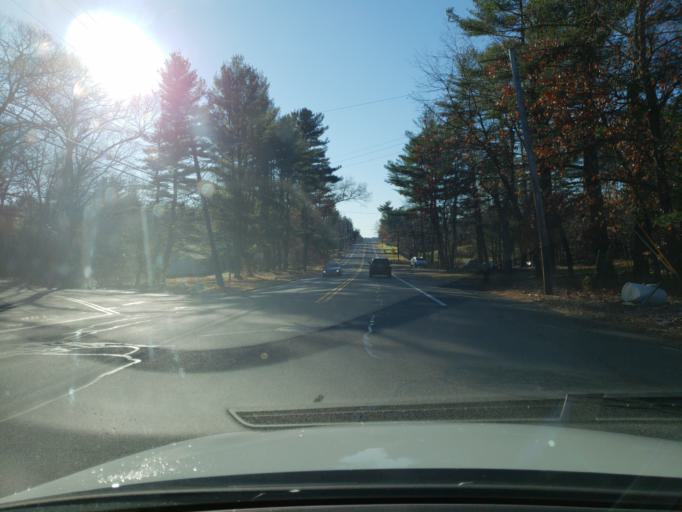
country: US
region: Massachusetts
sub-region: Essex County
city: Andover
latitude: 42.6113
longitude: -71.1235
